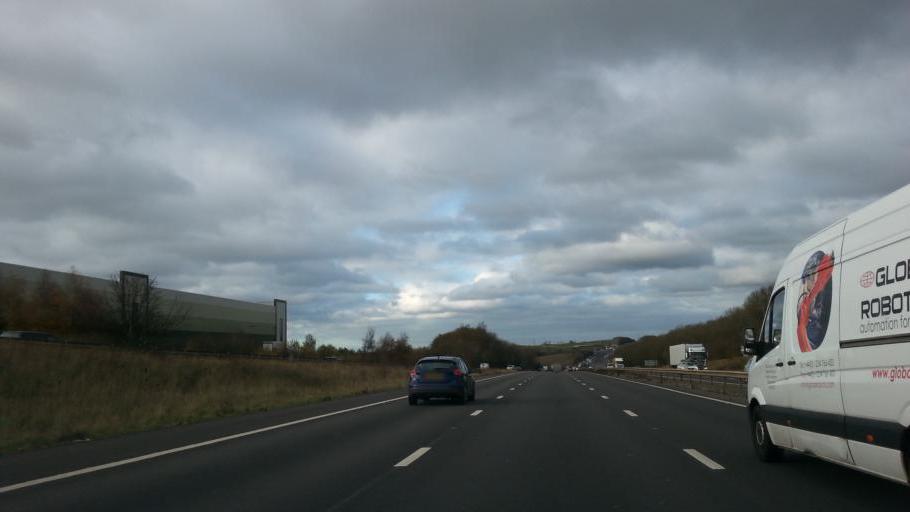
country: GB
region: England
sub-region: Warwickshire
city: Rugby
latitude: 52.4083
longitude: -1.2487
